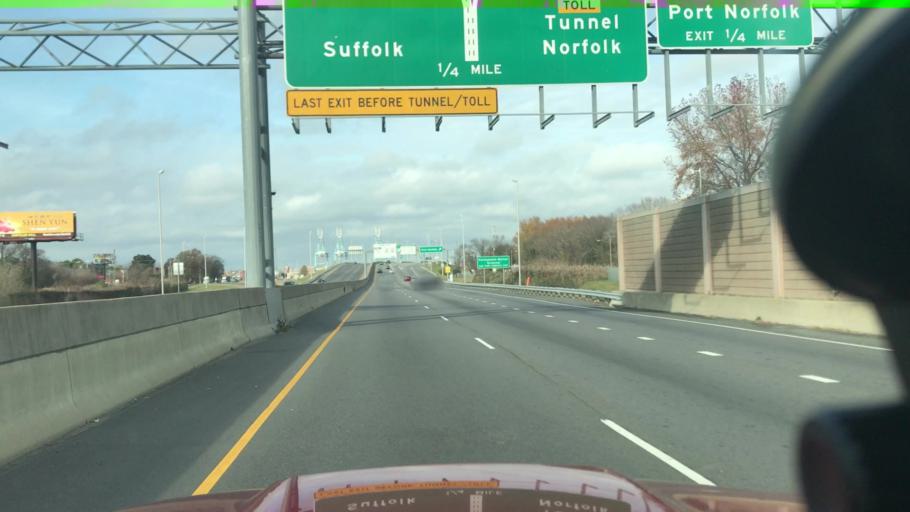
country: US
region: Virginia
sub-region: City of Portsmouth
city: Portsmouth
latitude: 36.8410
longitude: -76.3291
